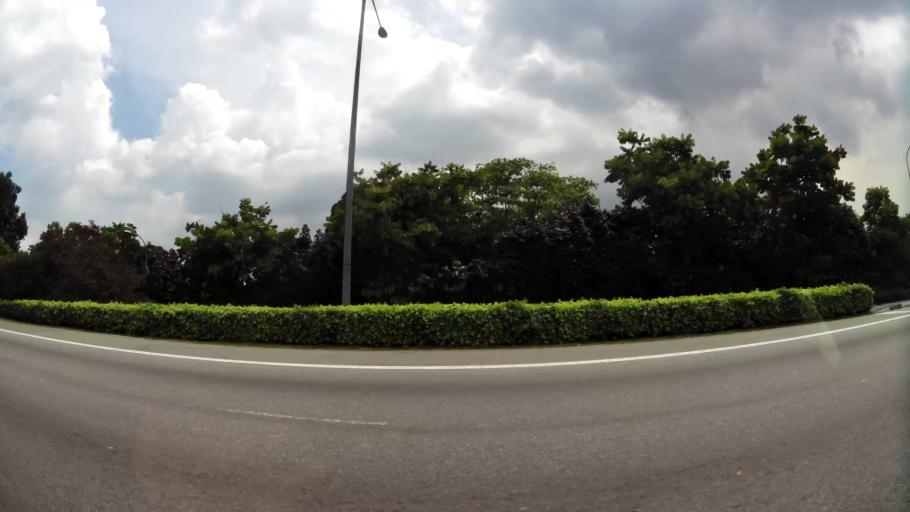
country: SG
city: Singapore
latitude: 1.3675
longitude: 103.8608
